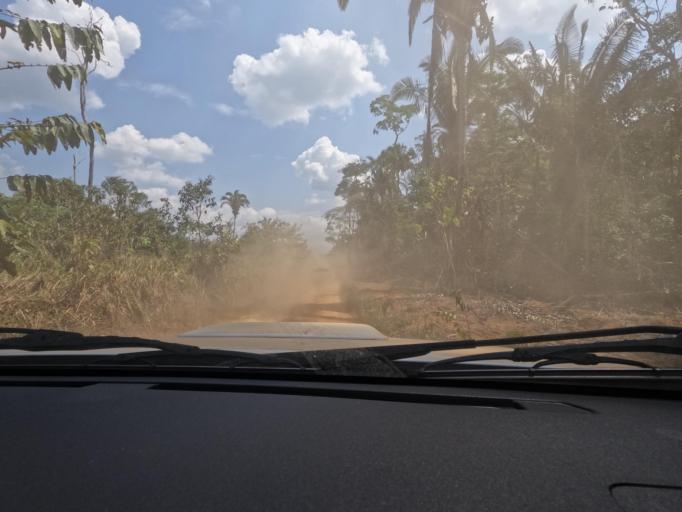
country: BR
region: Rondonia
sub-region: Porto Velho
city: Porto Velho
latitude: -8.6071
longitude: -64.2211
